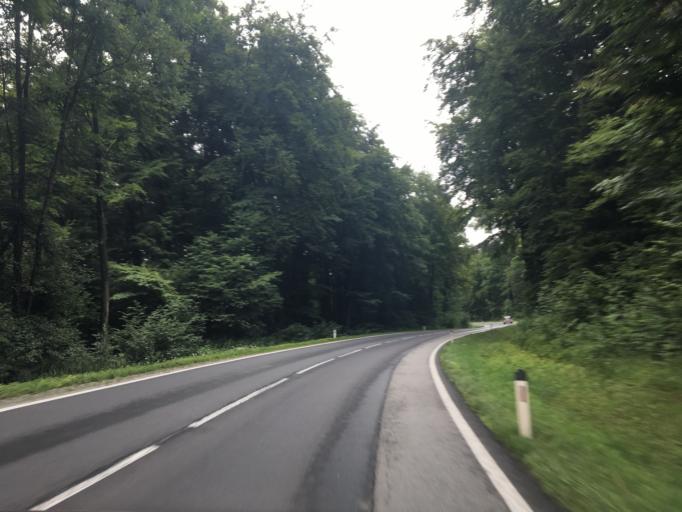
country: AT
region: Salzburg
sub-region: Politischer Bezirk Salzburg-Umgebung
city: Dorfbeuern
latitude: 48.1167
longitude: 13.0034
